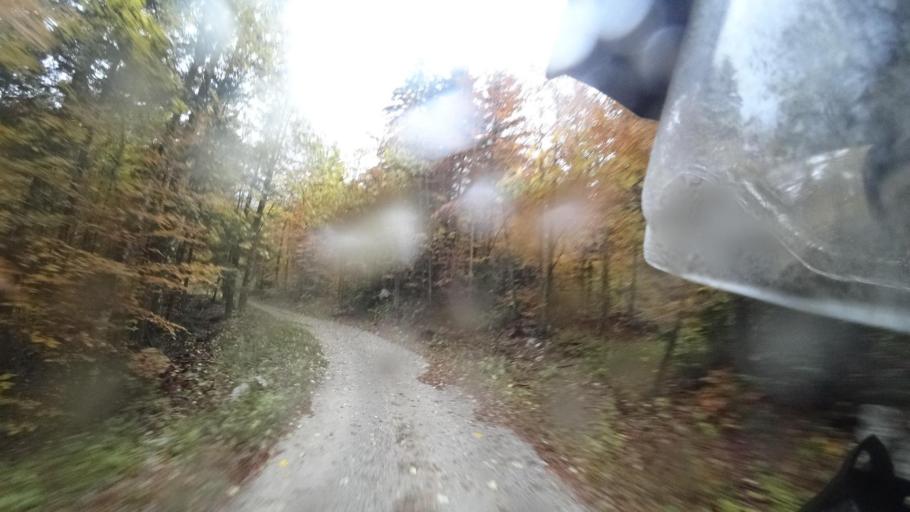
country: HR
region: Primorsko-Goranska
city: Vrbovsko
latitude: 45.2653
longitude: 14.9990
